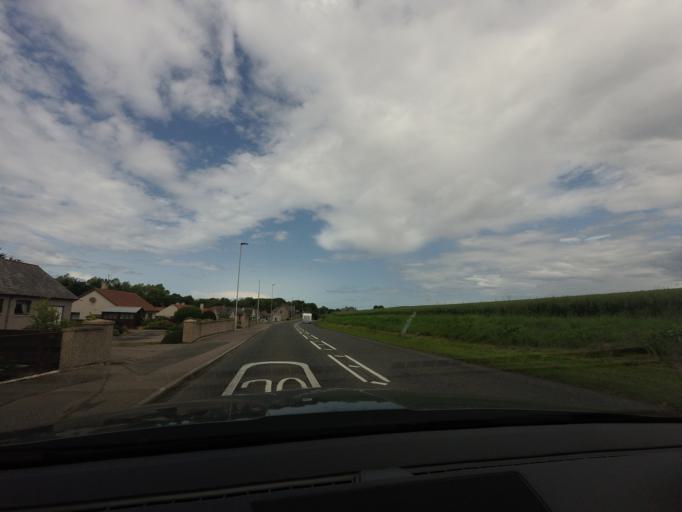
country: GB
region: Scotland
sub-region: Aberdeenshire
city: Portsoy
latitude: 57.6760
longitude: -2.6881
